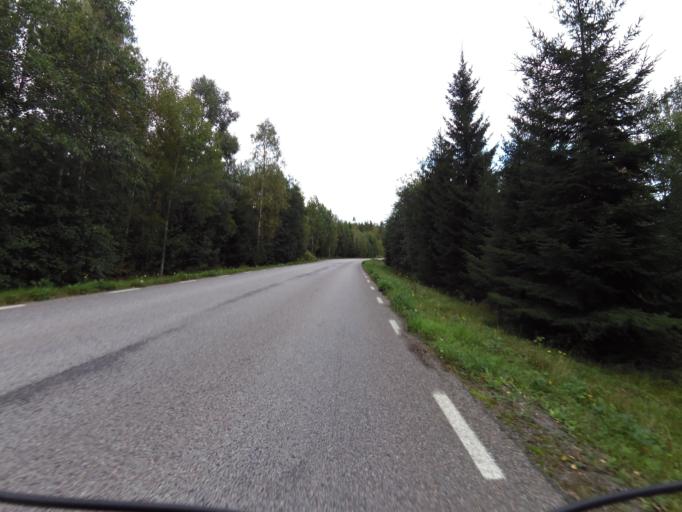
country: SE
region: Gaevleborg
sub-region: Sandvikens Kommun
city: Sandviken
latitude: 60.6499
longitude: 16.8247
